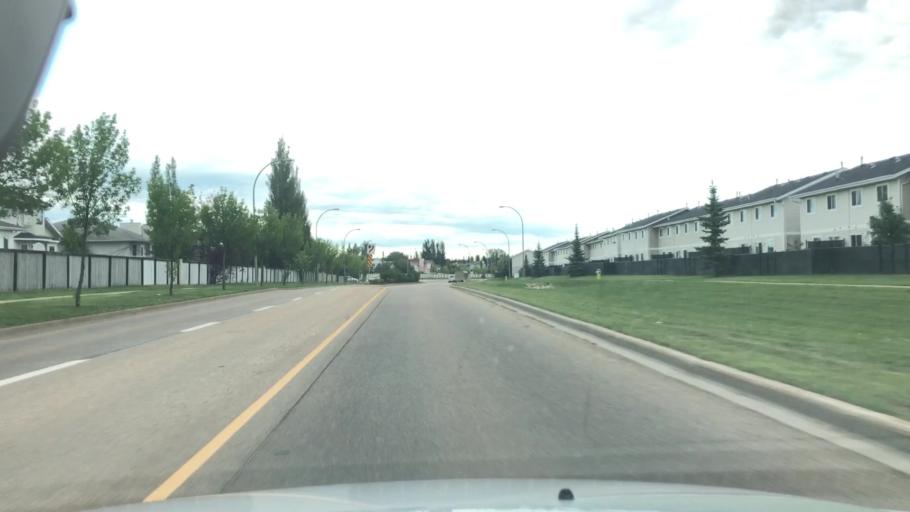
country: CA
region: Alberta
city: St. Albert
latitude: 53.6153
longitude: -113.5481
